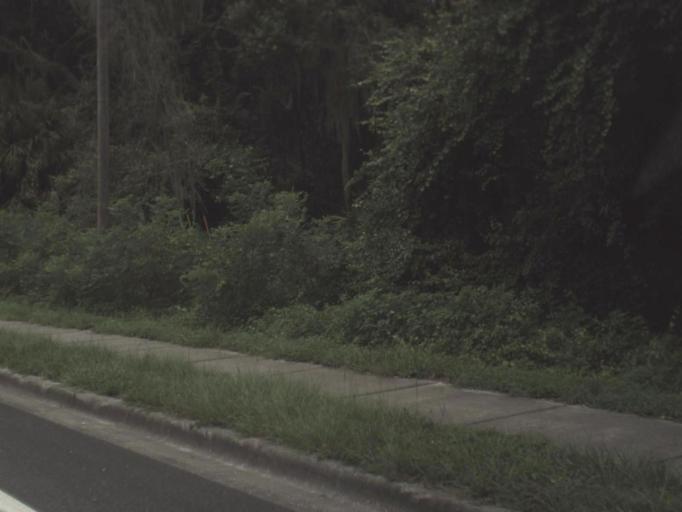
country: US
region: Florida
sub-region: Citrus County
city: Inverness
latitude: 28.8493
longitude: -82.2735
